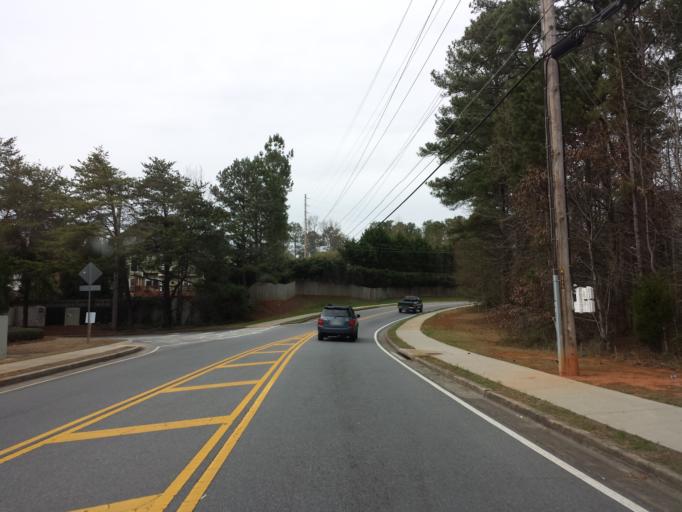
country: US
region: Georgia
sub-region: Fulton County
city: Roswell
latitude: 34.0285
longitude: -84.4198
